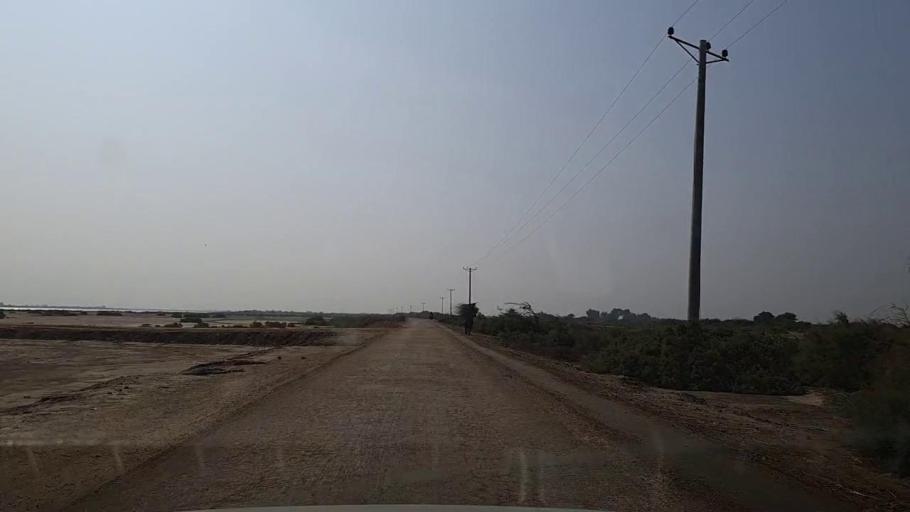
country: PK
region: Sindh
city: Mirpur Sakro
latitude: 24.5400
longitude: 67.6014
